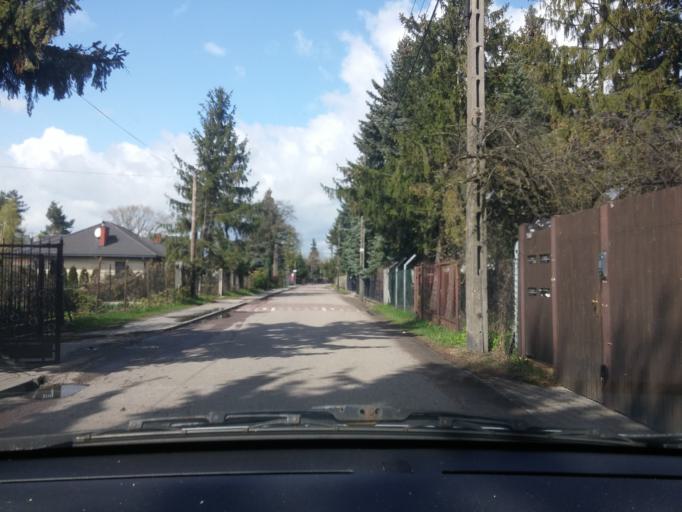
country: PL
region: Masovian Voivodeship
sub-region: Warszawa
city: Wawer
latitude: 52.1992
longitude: 21.1301
